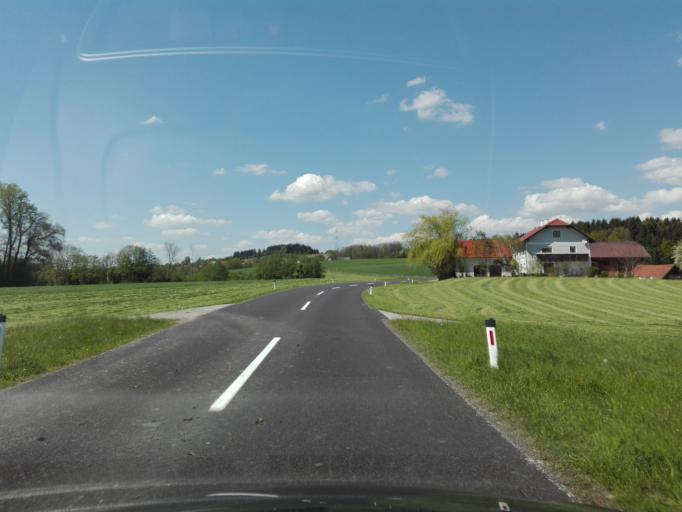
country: AT
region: Upper Austria
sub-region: Politischer Bezirk Urfahr-Umgebung
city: Feldkirchen an der Donau
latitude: 48.3542
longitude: 13.9407
